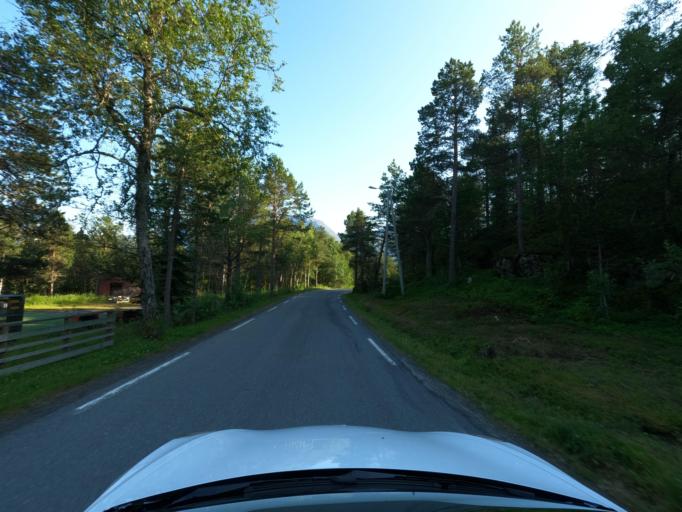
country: NO
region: Nordland
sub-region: Narvik
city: Bjerkvik
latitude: 68.4786
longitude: 17.5281
